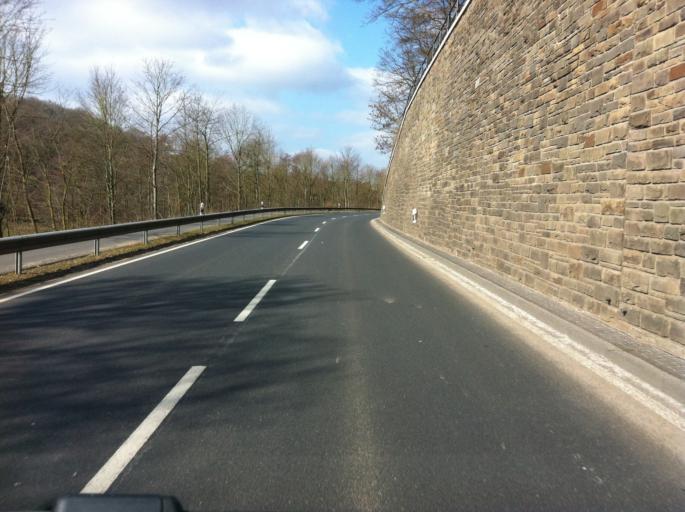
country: DE
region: North Rhine-Westphalia
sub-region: Regierungsbezirk Koln
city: Bad Munstereifel
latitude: 50.5395
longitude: 6.7688
